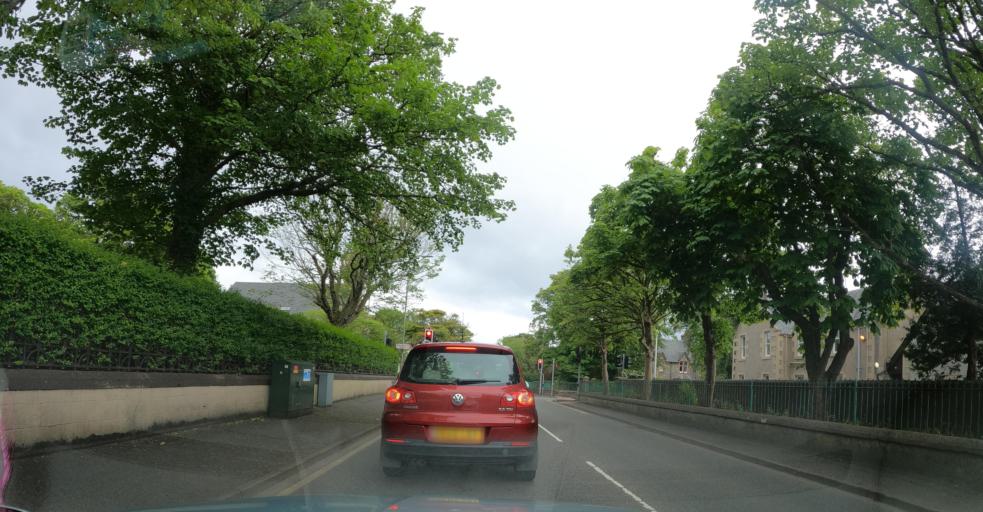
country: GB
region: Scotland
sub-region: Eilean Siar
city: Stornoway
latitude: 58.2113
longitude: -6.3828
